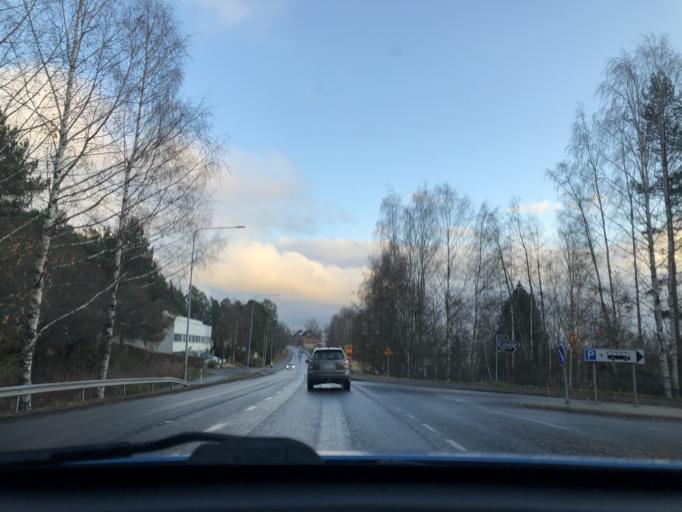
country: FI
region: Pirkanmaa
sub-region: Tampere
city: Kangasala
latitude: 61.4658
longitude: 24.0544
